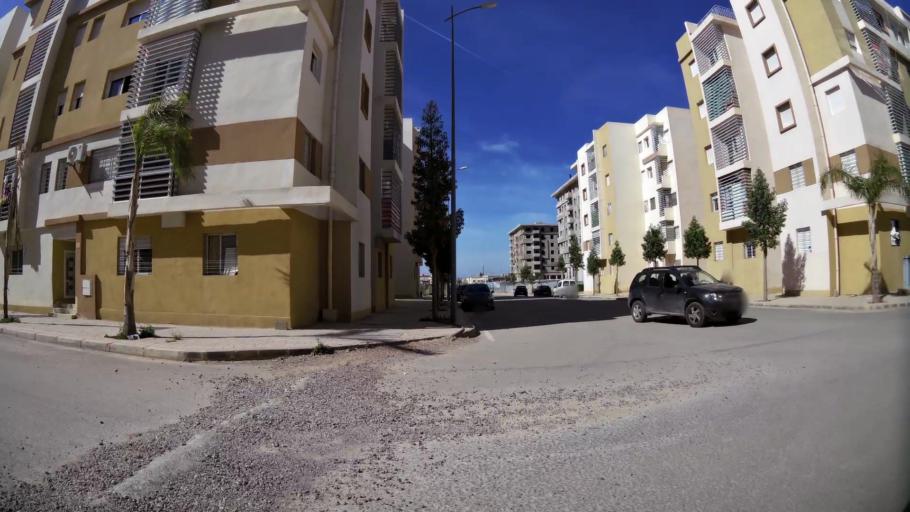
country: MA
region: Oriental
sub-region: Oujda-Angad
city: Oujda
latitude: 34.6628
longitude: -1.9145
